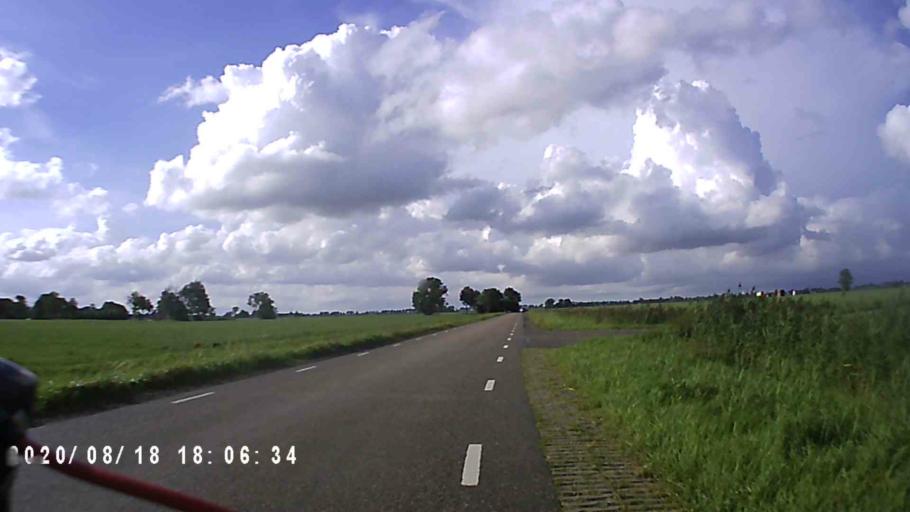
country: NL
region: Groningen
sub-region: Gemeente Zuidhorn
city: Noordhorn
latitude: 53.2800
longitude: 6.3905
